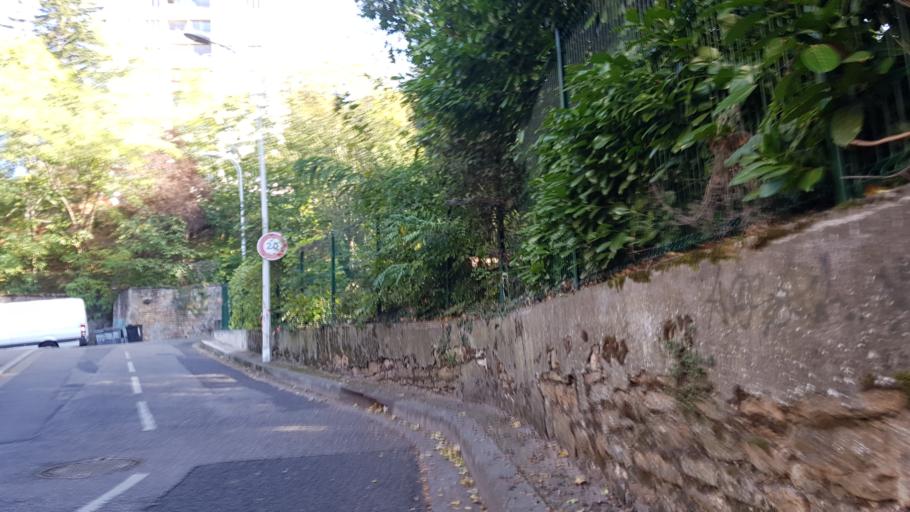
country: FR
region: Rhone-Alpes
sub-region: Departement du Rhone
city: Caluire-et-Cuire
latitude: 45.7822
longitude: 4.8144
